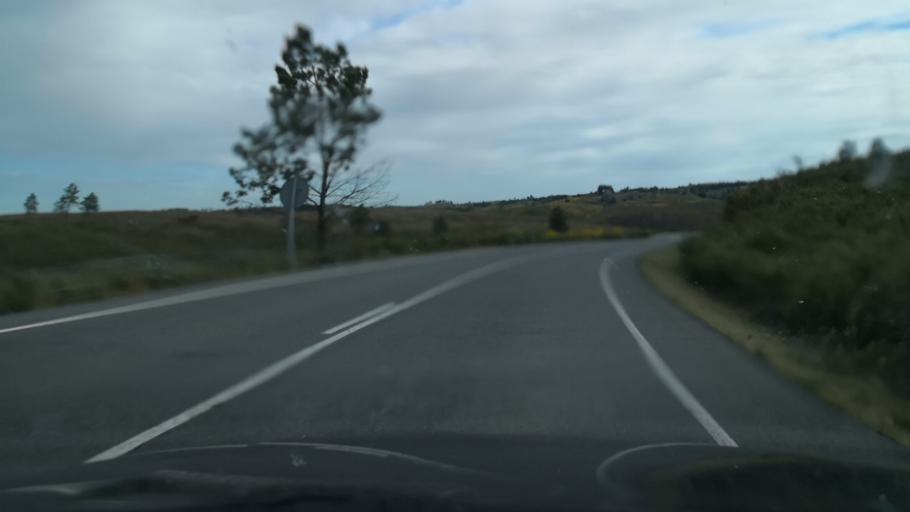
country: ES
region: Extremadura
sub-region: Provincia de Caceres
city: Perales del Puerto
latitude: 40.1760
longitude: -6.6748
